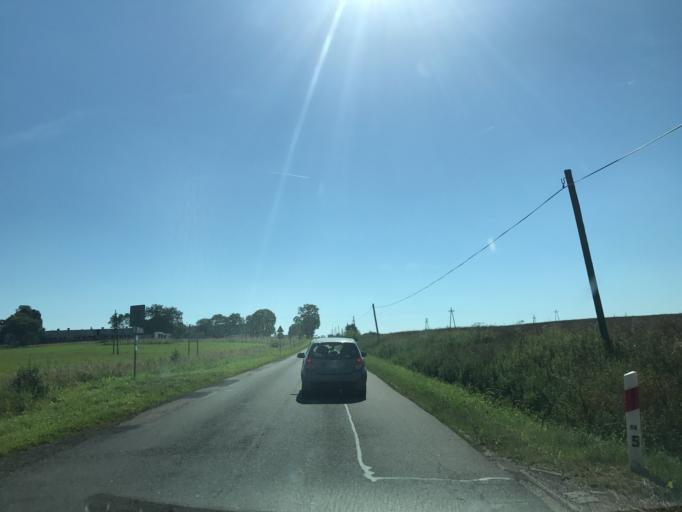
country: PL
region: Pomeranian Voivodeship
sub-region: Powiat bytowski
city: Czarna Dabrowka
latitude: 54.3663
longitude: 17.5062
